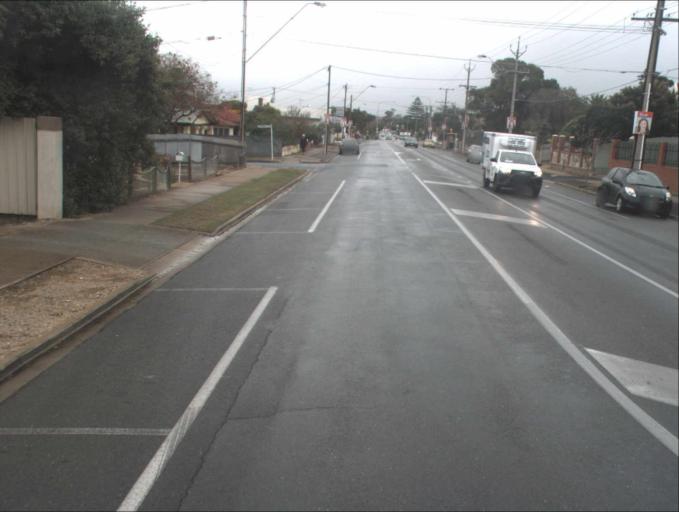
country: AU
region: South Australia
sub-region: Prospect
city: Prospect
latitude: -34.8706
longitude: 138.5929
